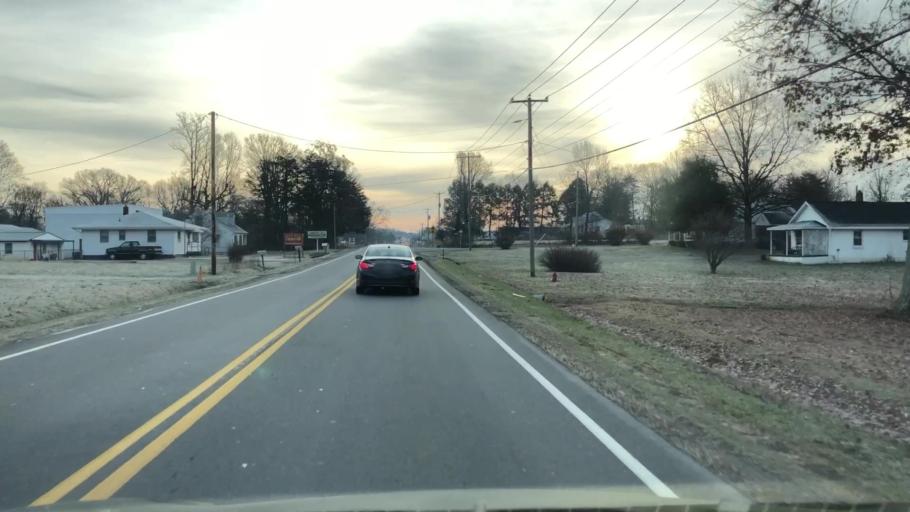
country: US
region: Virginia
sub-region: Campbell County
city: Timberlake
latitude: 37.3323
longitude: -79.2563
